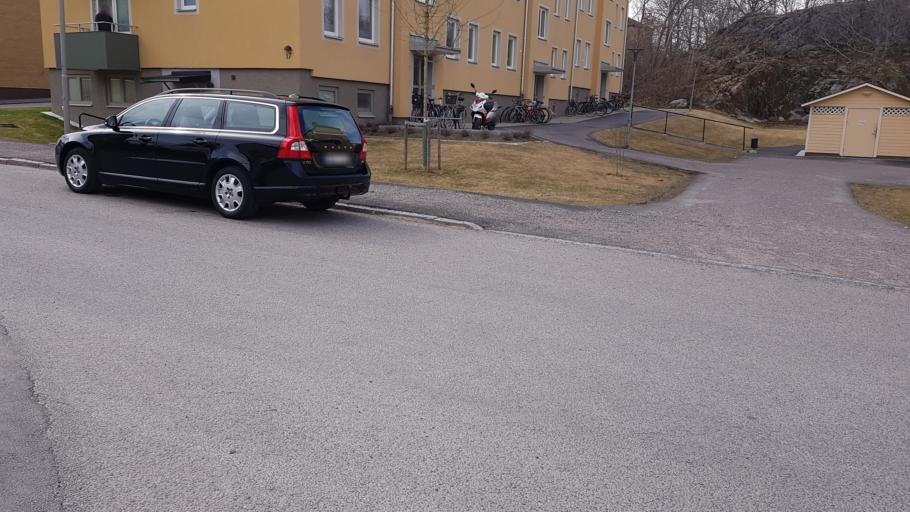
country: SE
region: OEstergoetland
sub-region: Norrkopings Kommun
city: Norrkoping
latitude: 58.5885
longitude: 16.2108
